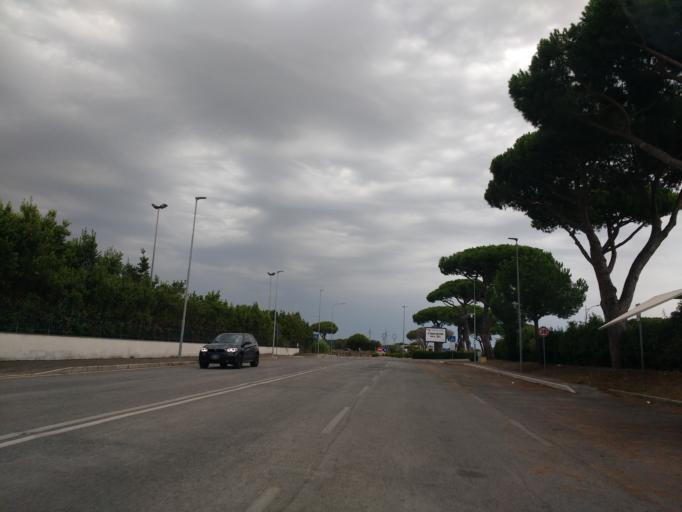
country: IT
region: Latium
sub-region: Citta metropolitana di Roma Capitale
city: Monte Migliore-La Selvotta
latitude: 41.7156
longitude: 12.4499
